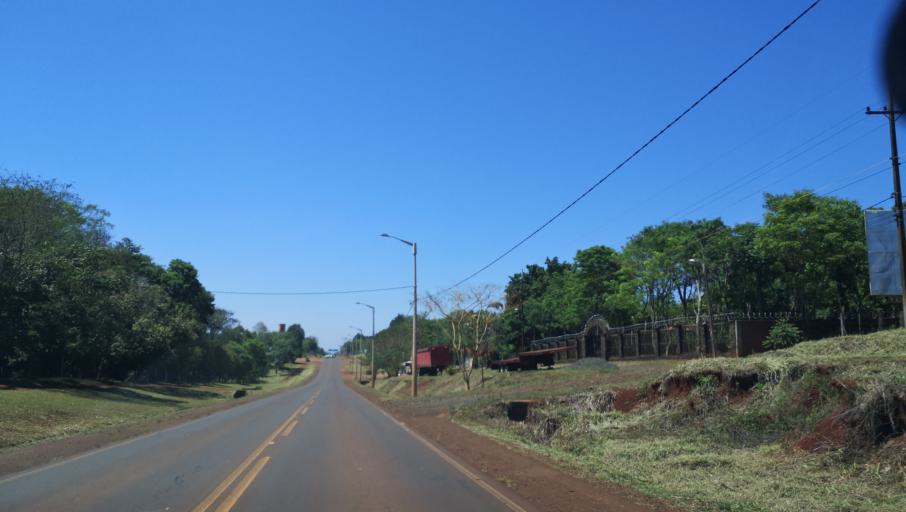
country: PY
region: Itapua
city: San Juan del Parana
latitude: -27.2757
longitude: -55.9503
